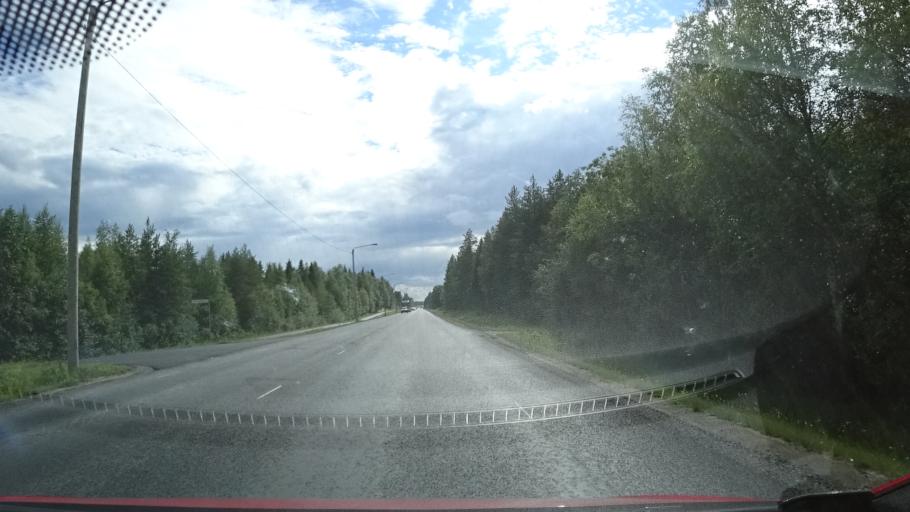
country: FI
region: Lapland
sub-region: Rovaniemi
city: Rovaniemi
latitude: 66.4578
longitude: 25.5875
